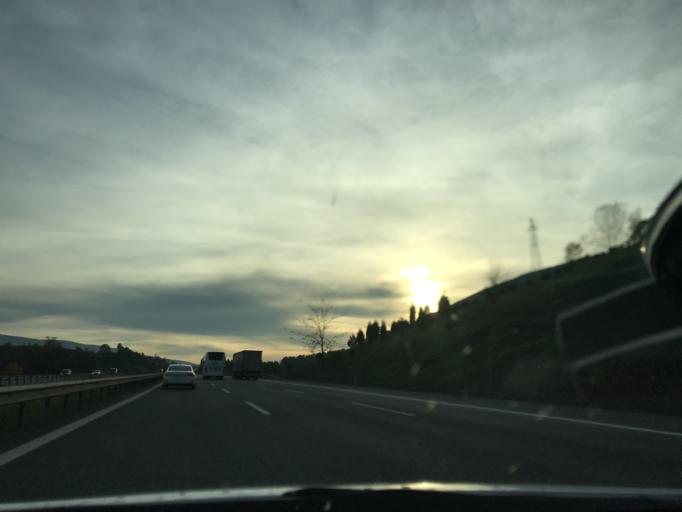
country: TR
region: Duzce
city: Gumusova
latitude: 40.8230
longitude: 30.9187
